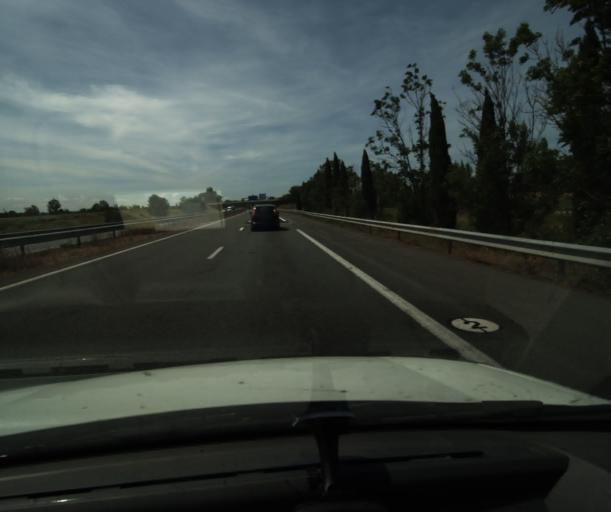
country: FR
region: Languedoc-Roussillon
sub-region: Departement de l'Aude
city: Bram
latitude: 43.2340
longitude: 2.1042
